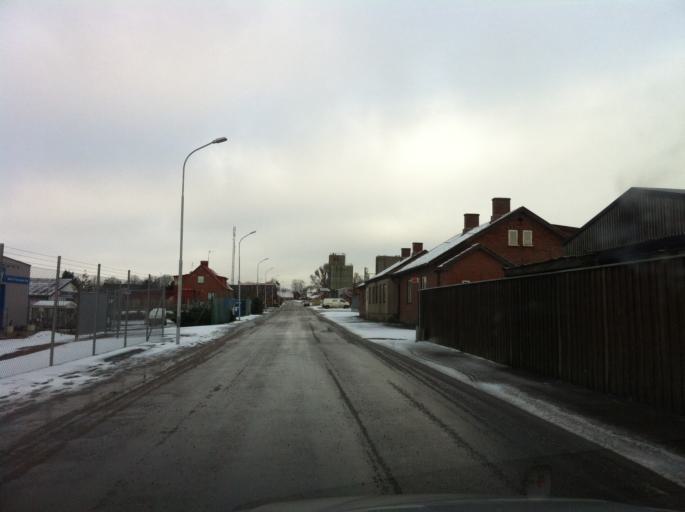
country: SE
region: Skane
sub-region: Svalovs Kommun
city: Svaloev
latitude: 55.9060
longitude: 13.1076
